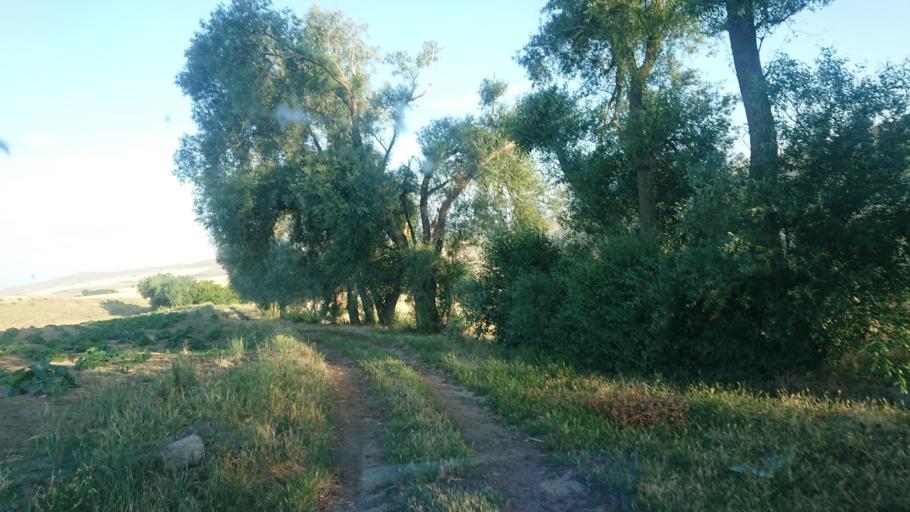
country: TR
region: Aksaray
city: Agacoren
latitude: 38.8323
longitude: 33.8845
